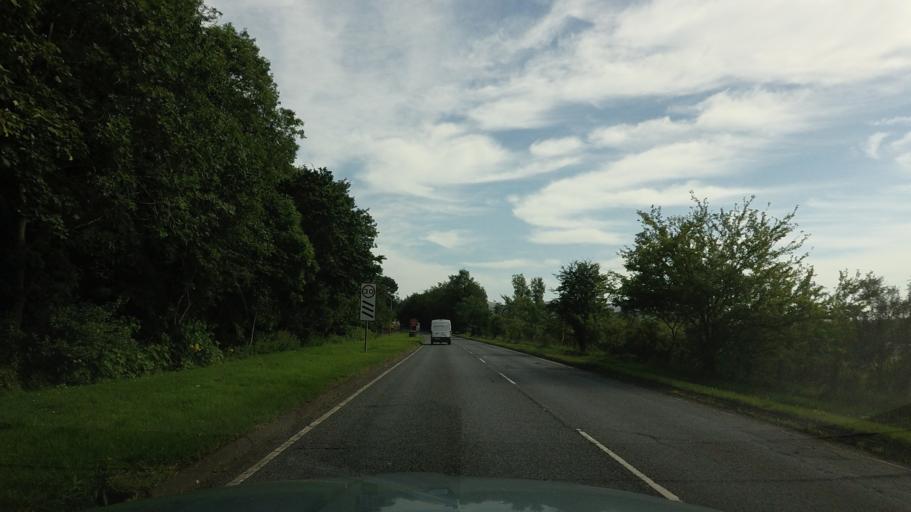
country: GB
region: Scotland
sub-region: The Scottish Borders
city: Peebles
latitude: 55.6655
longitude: -3.1952
